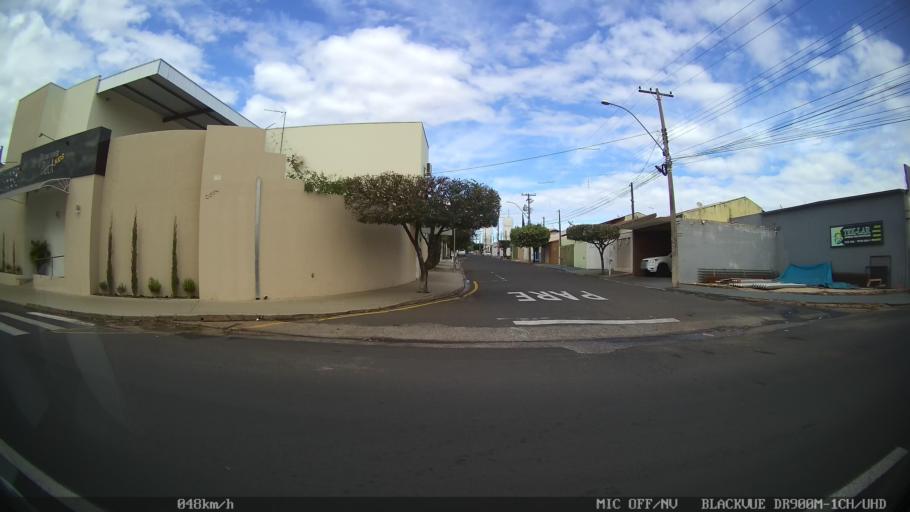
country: BR
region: Sao Paulo
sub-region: Sao Jose Do Rio Preto
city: Sao Jose do Rio Preto
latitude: -20.8047
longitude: -49.4949
